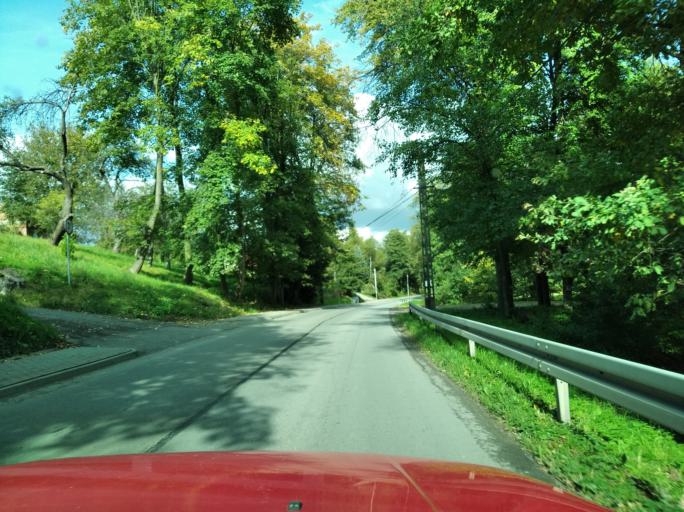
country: PL
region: Subcarpathian Voivodeship
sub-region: Powiat rzeszowski
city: Tyczyn
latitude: 49.9437
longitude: 22.0214
